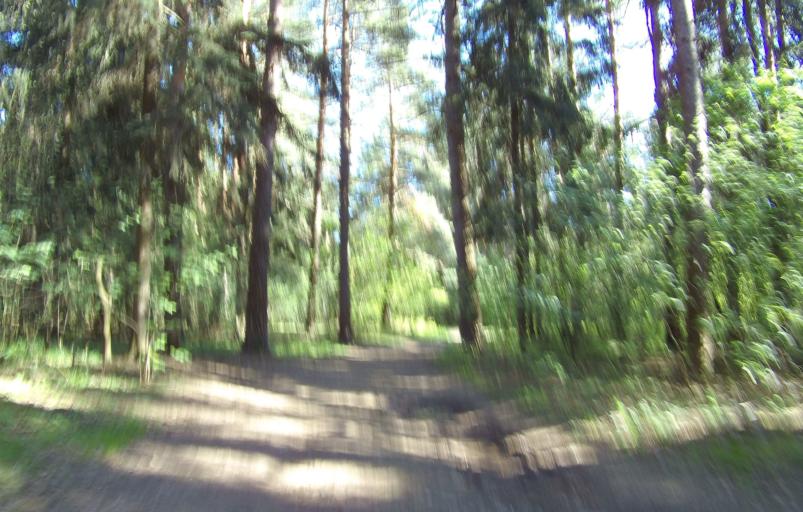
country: RU
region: Moskovskaya
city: Kratovo
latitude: 55.5644
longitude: 38.1842
